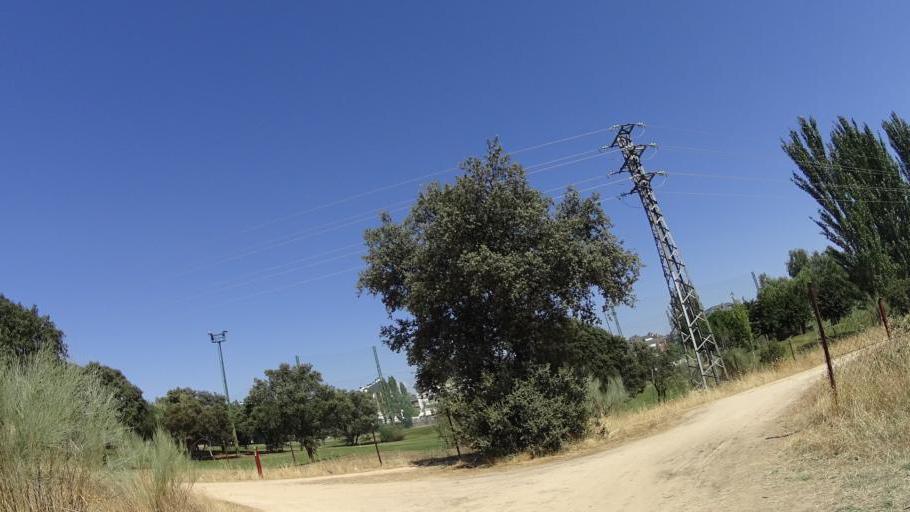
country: ES
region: Madrid
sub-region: Provincia de Madrid
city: Majadahonda
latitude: 40.4437
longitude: -3.8654
